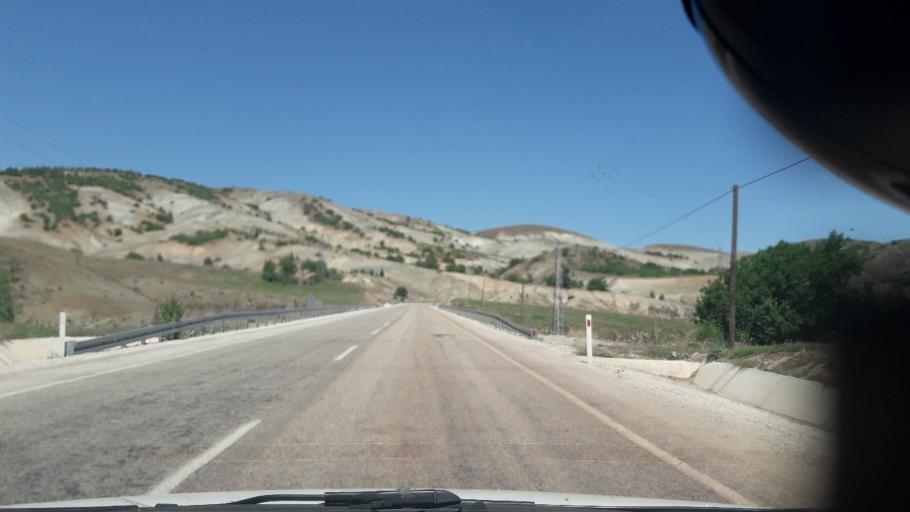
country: TR
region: Malatya
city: Hekimhan
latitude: 38.8285
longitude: 37.8625
